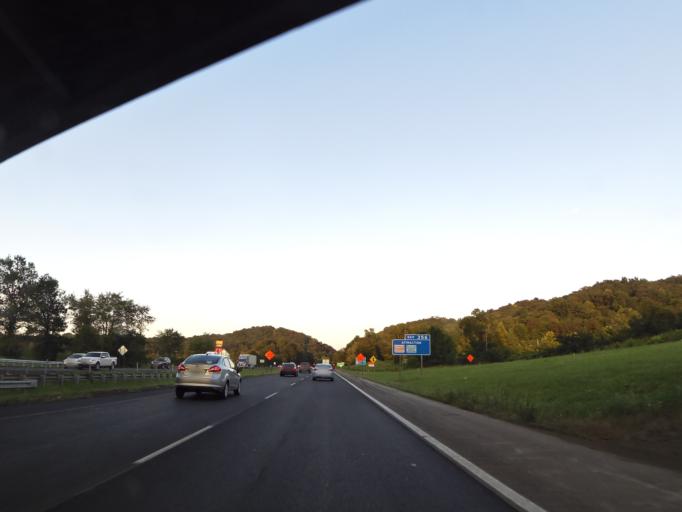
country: US
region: Tennessee
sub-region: Roane County
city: Kingston
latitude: 35.8731
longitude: -84.4621
